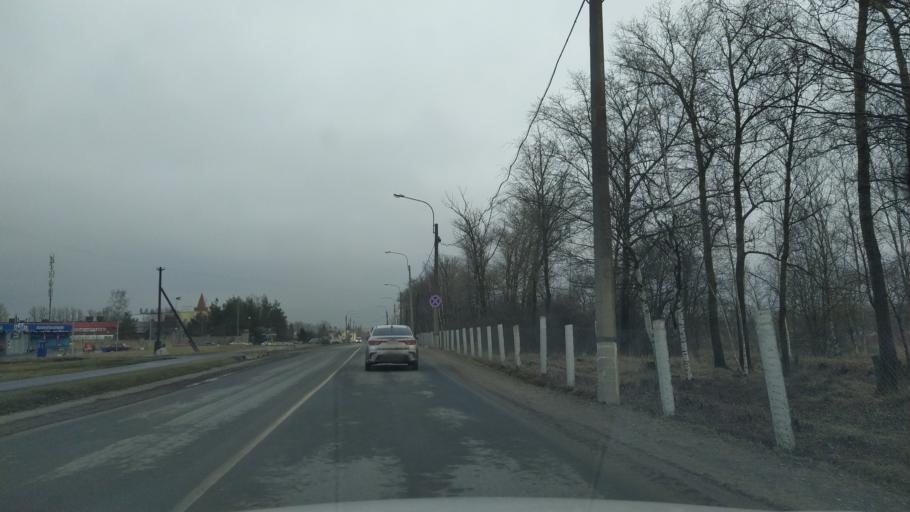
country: RU
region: St.-Petersburg
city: Pushkin
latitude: 59.7317
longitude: 30.3726
